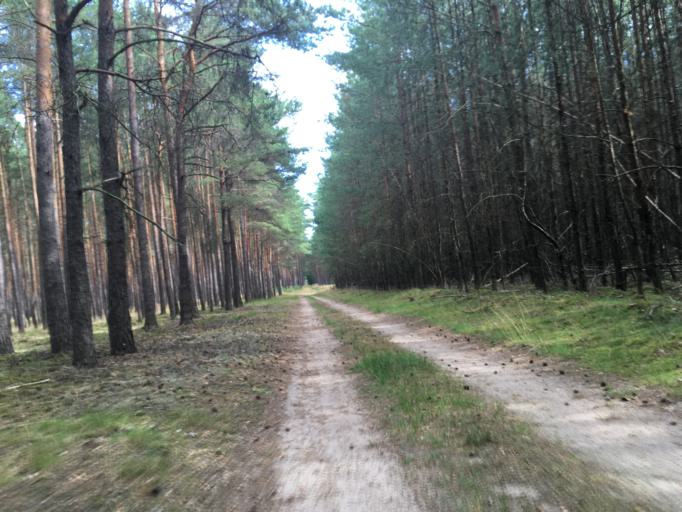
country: DE
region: Brandenburg
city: Rheinsberg
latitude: 53.0322
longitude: 12.9314
